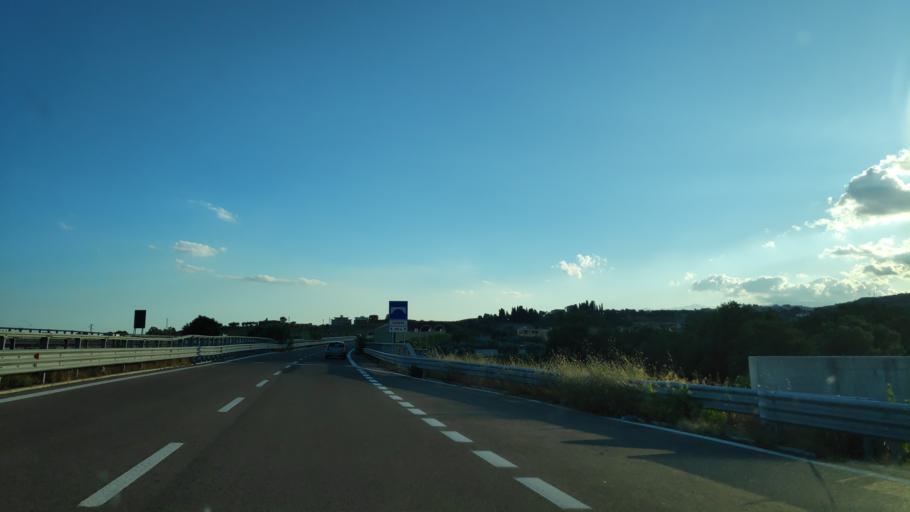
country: IT
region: Calabria
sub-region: Provincia di Reggio Calabria
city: Locri
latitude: 38.2504
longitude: 16.2571
